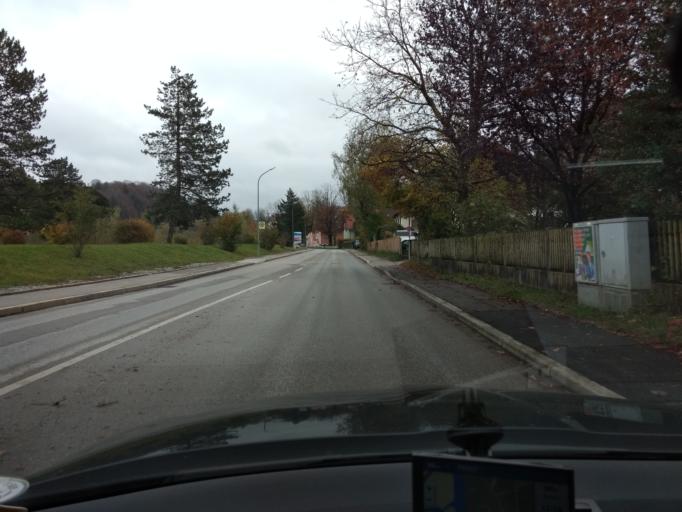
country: DE
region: Bavaria
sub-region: Upper Bavaria
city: Bad Toelz
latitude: 47.7636
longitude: 11.5432
